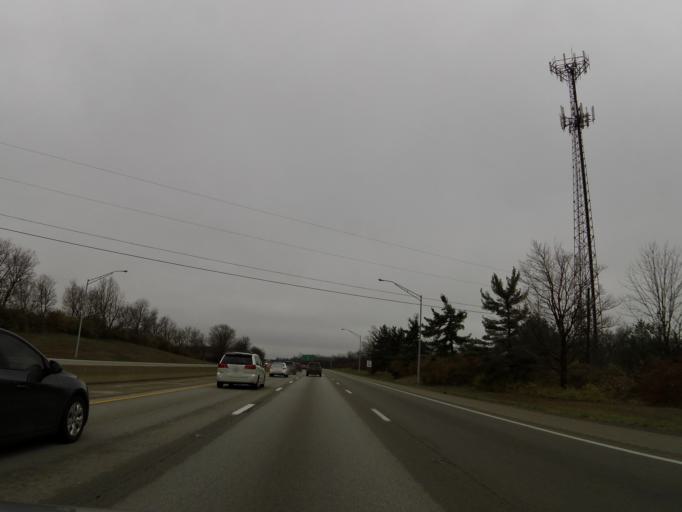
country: US
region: Kentucky
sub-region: Scott County
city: Georgetown
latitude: 38.1393
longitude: -84.5299
